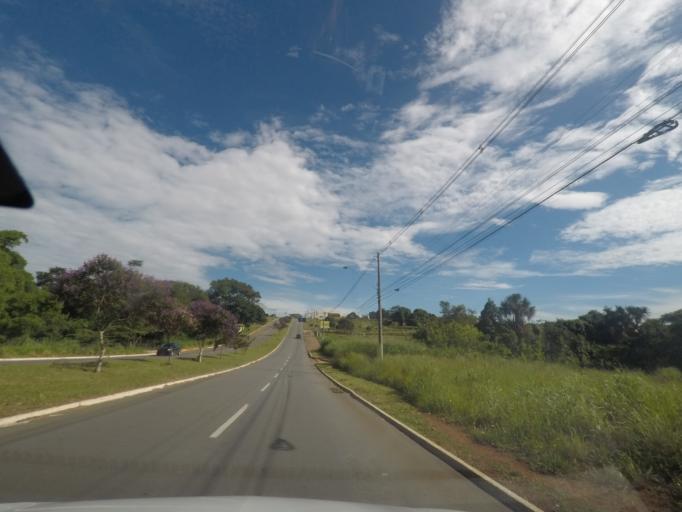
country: BR
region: Goias
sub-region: Aparecida De Goiania
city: Aparecida de Goiania
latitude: -16.8157
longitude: -49.2797
